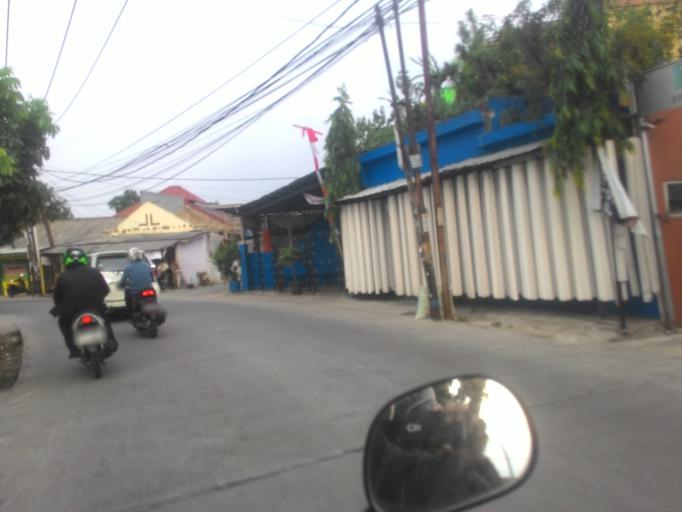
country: ID
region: West Java
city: Depok
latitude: -6.3624
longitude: 106.8161
